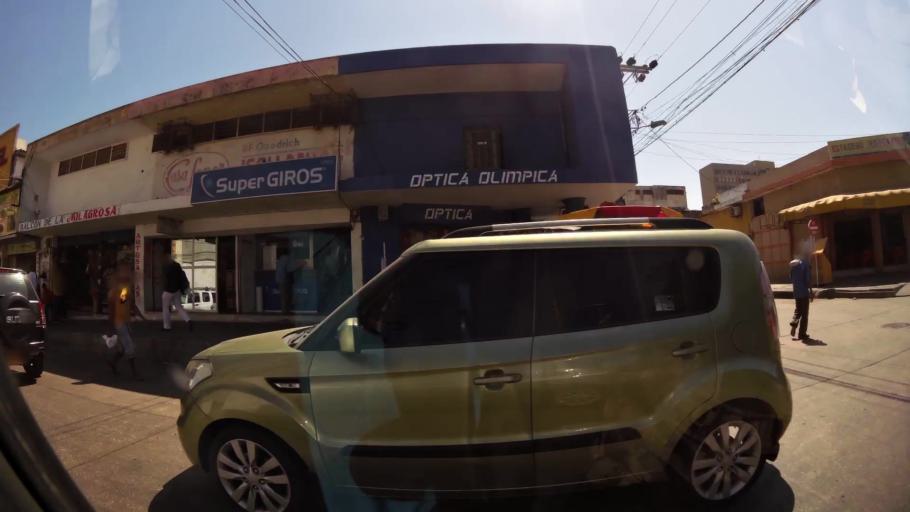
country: CO
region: Atlantico
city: Barranquilla
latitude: 10.9838
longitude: -74.7822
